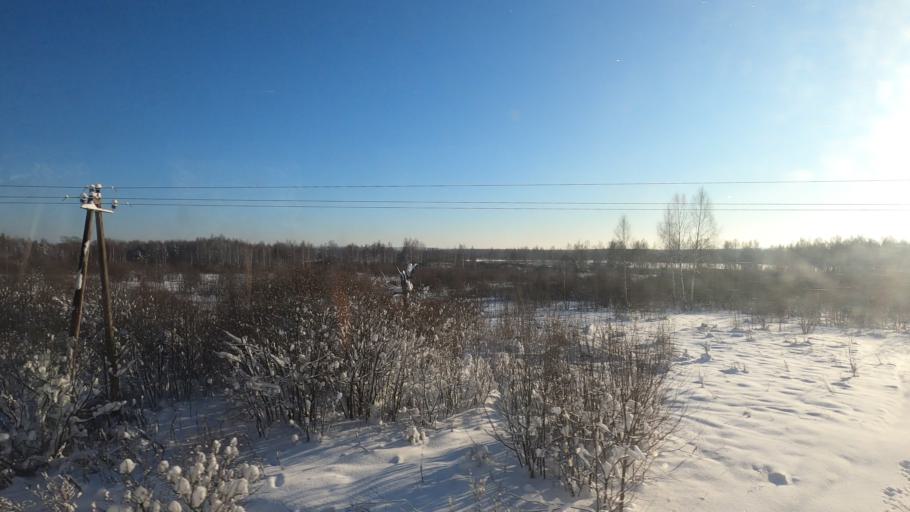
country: RU
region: Moskovskaya
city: Zhukovka
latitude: 56.4748
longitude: 37.5416
